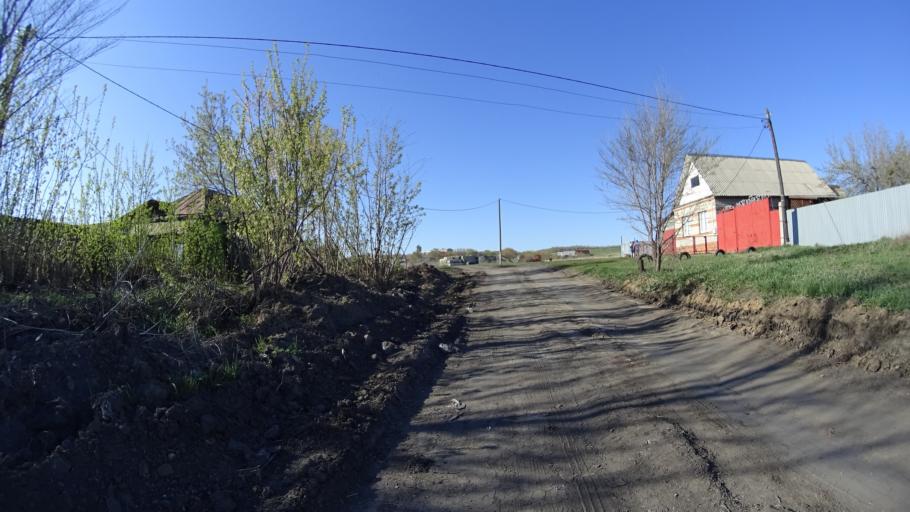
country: RU
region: Chelyabinsk
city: Troitsk
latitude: 54.0935
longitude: 61.5998
